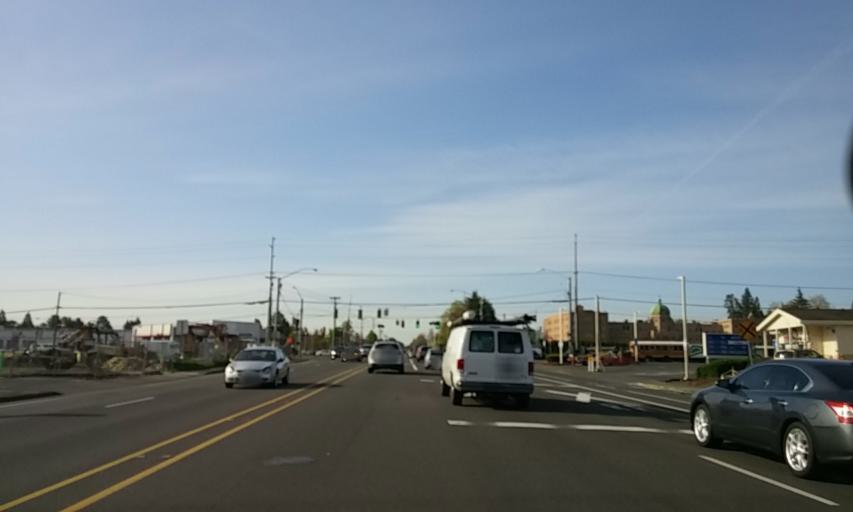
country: US
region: Oregon
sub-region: Washington County
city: Beaverton
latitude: 45.4906
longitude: -122.8262
